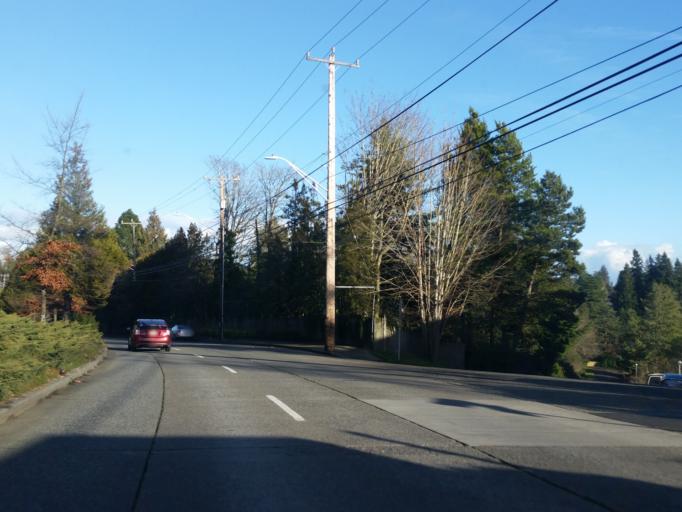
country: US
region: Washington
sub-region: King County
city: Yarrow Point
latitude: 47.6685
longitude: -122.2734
